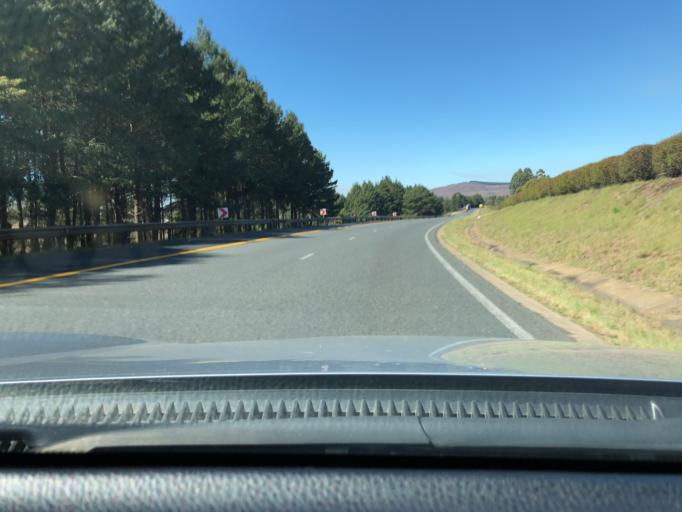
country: ZA
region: KwaZulu-Natal
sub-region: uMgungundlovu District Municipality
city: Mooirivier
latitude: -29.3438
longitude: 30.0822
